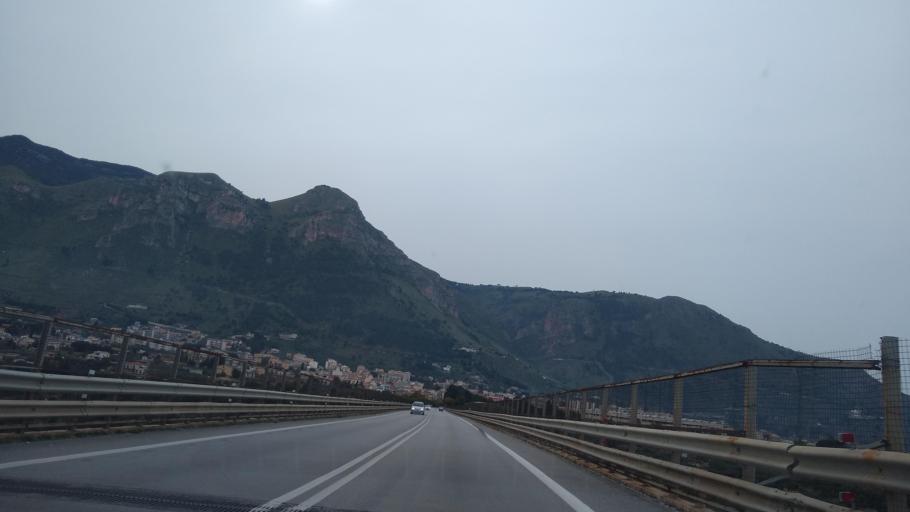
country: IT
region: Sicily
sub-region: Trapani
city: Castellammare del Golfo
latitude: 38.0157
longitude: 12.9013
